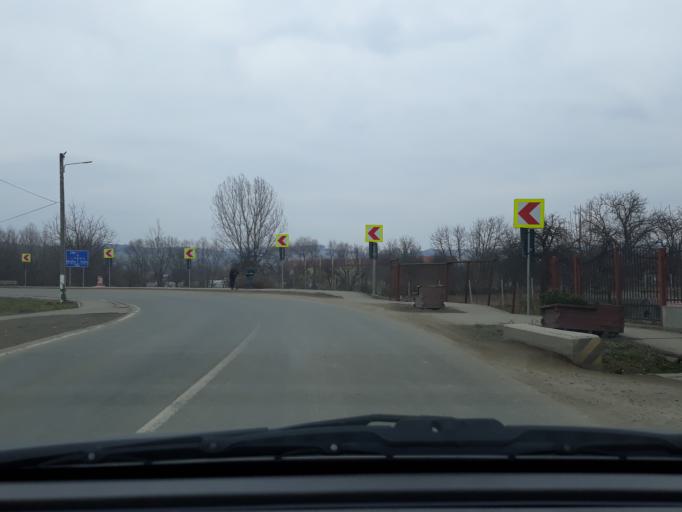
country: RO
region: Salaj
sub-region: Comuna Nusfalau
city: Nusfalau
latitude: 47.1978
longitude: 22.7070
